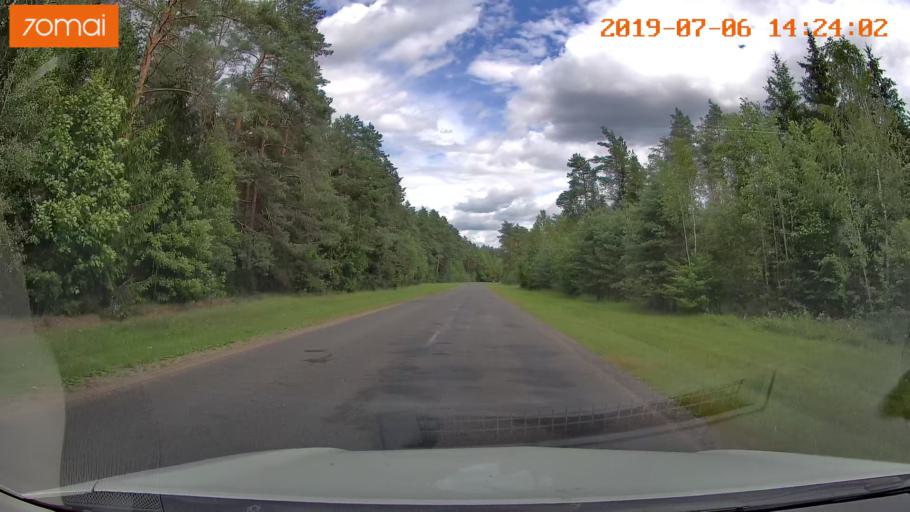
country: BY
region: Minsk
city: Ivyanyets
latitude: 53.9208
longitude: 26.7746
